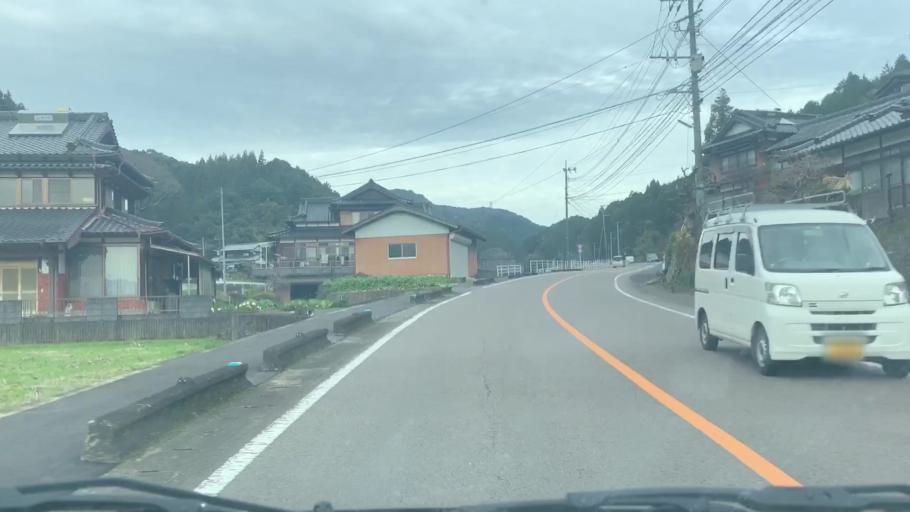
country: JP
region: Saga Prefecture
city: Ureshinomachi-shimojuku
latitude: 33.1532
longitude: 129.9730
